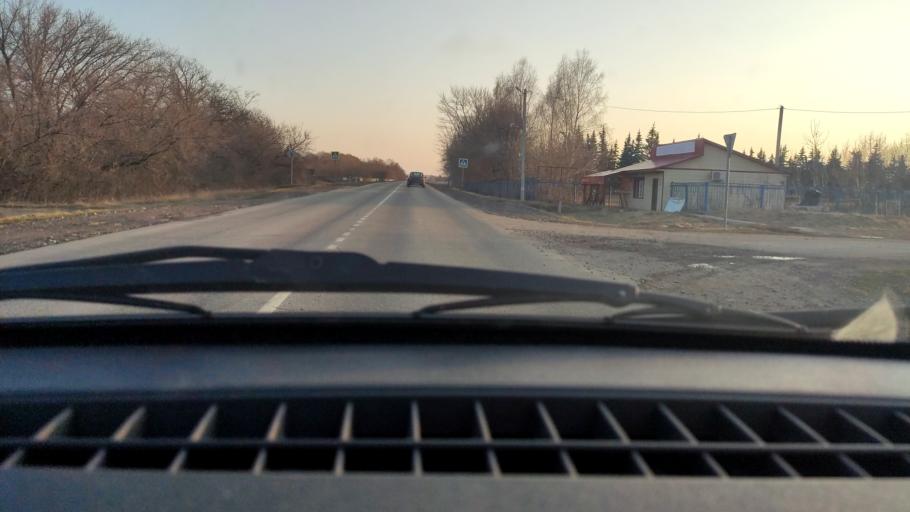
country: RU
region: Bashkortostan
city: Davlekanovo
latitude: 54.2960
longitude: 55.1268
